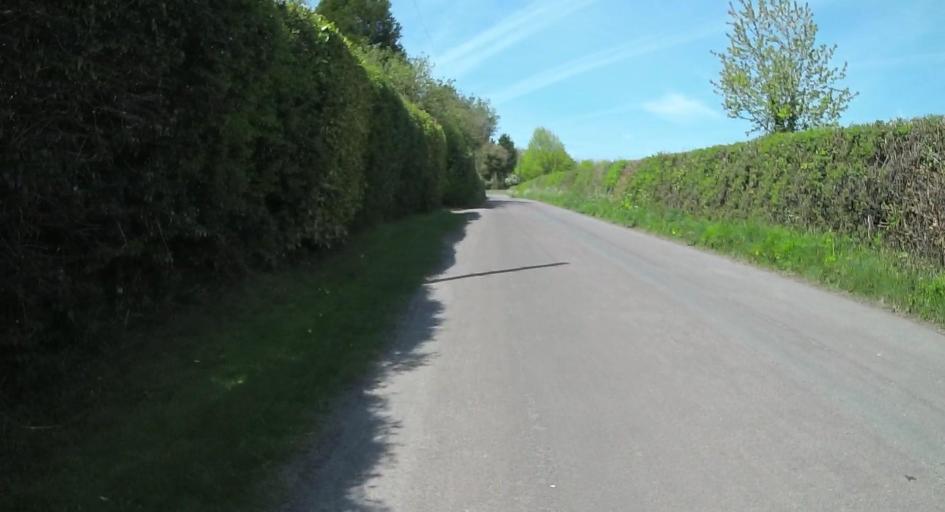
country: GB
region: England
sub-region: Hampshire
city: Romsey
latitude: 51.0817
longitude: -1.4799
